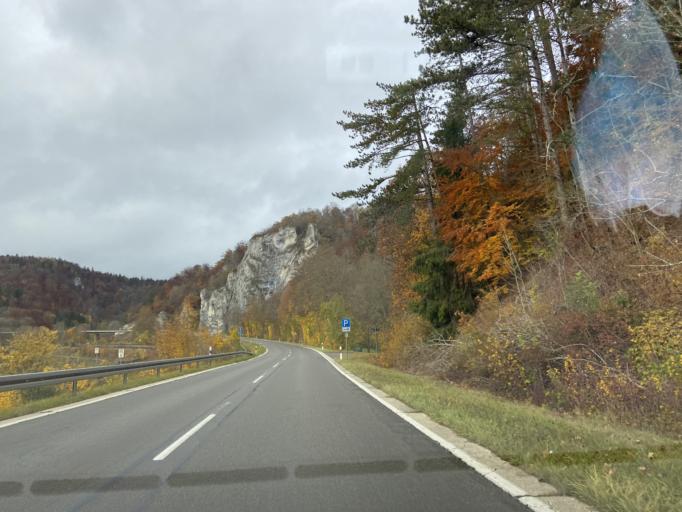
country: DE
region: Baden-Wuerttemberg
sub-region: Tuebingen Region
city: Inzigkofen
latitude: 48.0775
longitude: 9.1583
